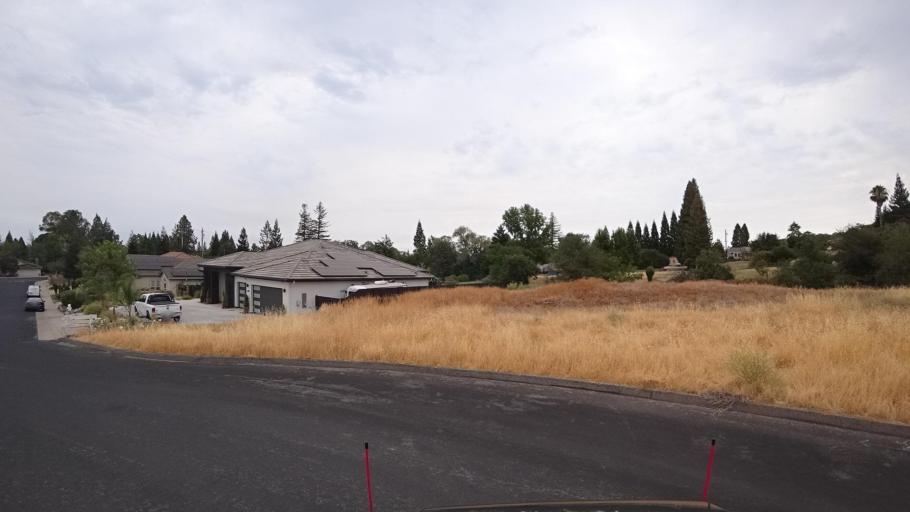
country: US
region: California
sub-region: Placer County
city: Rocklin
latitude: 38.7800
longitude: -121.2179
